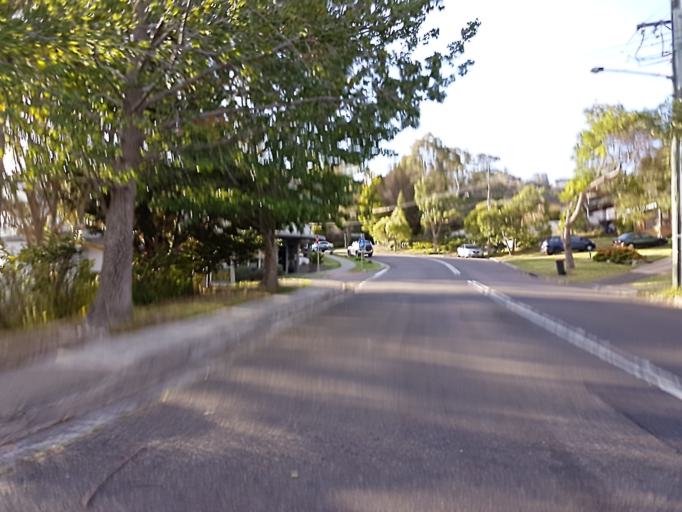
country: AU
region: New South Wales
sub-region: Warringah
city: Davidson
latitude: -33.7456
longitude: 151.2163
